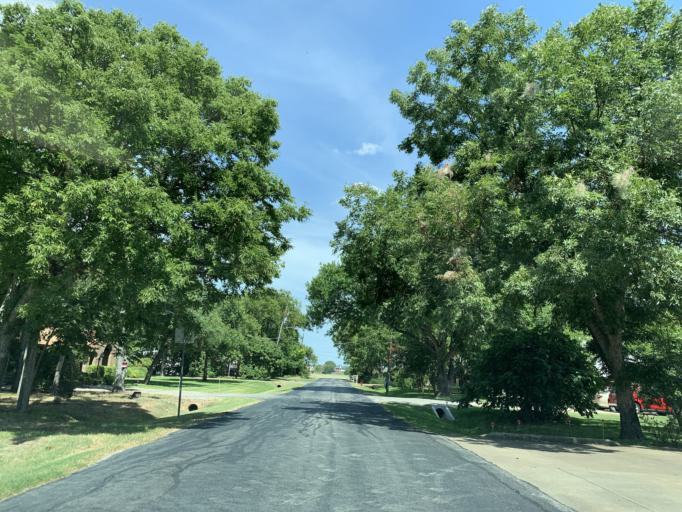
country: US
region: Texas
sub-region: Dallas County
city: Cedar Hill
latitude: 32.6488
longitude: -97.0162
